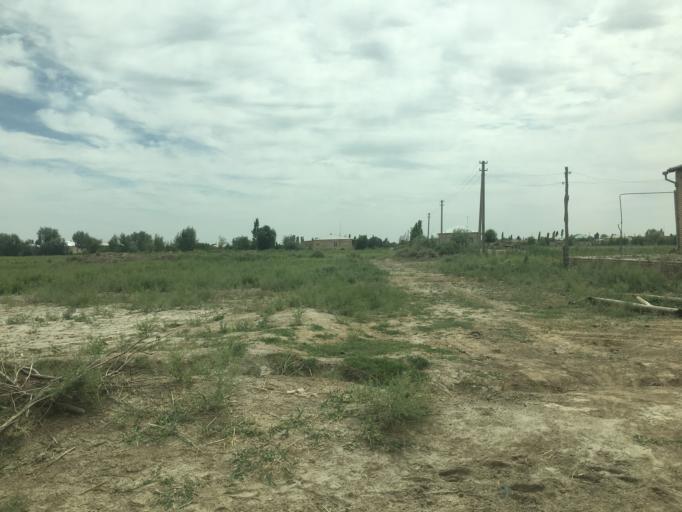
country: TM
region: Dasoguz
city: Tagta
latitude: 41.6130
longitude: 59.8169
